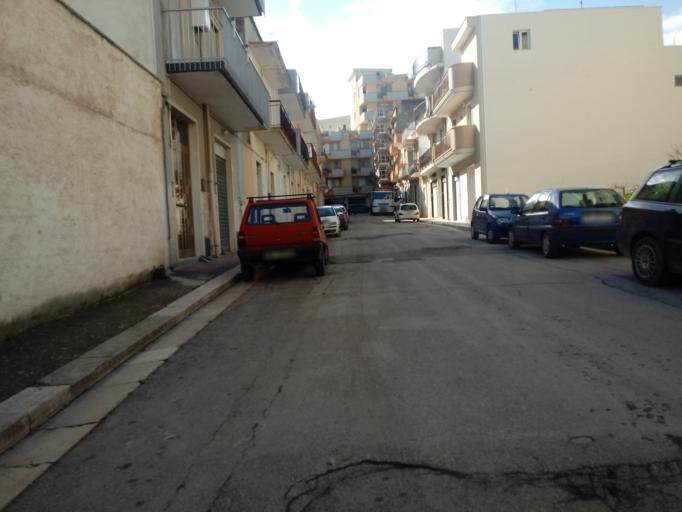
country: IT
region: Apulia
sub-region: Provincia di Barletta - Andria - Trani
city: Andria
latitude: 41.2195
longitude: 16.2948
